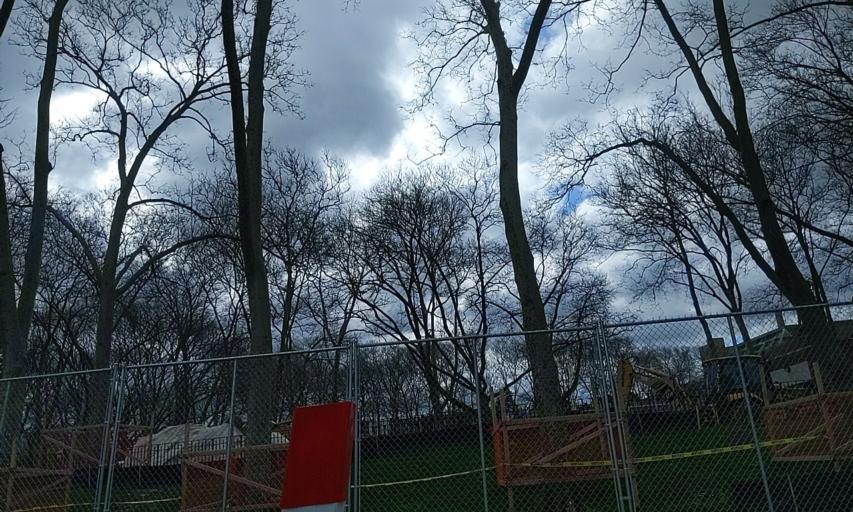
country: US
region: New York
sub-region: New York County
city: Manhattan
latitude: 40.7800
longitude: -73.9228
